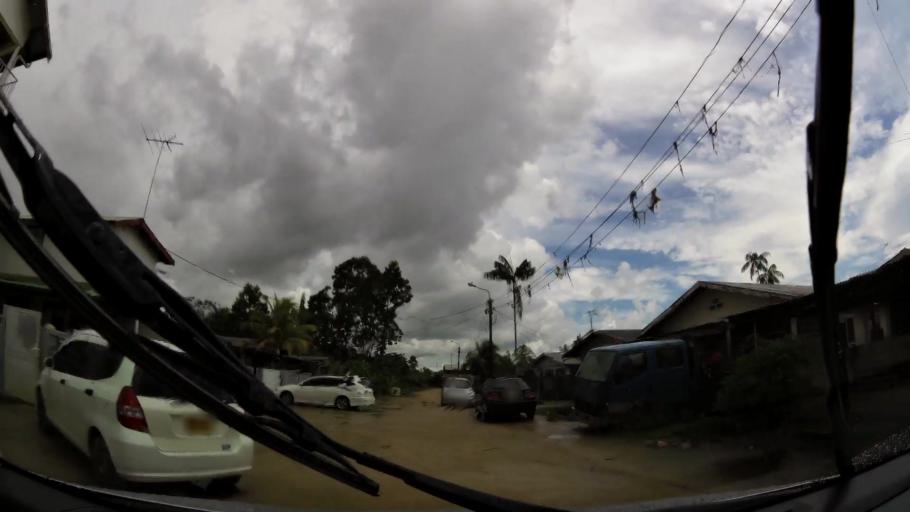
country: SR
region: Paramaribo
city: Paramaribo
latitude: 5.7896
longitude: -55.2004
